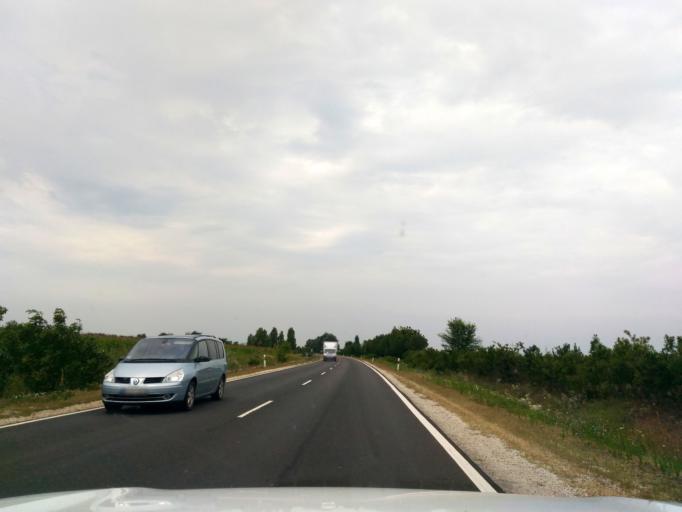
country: HU
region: Pest
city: Abony
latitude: 47.2060
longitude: 20.0720
